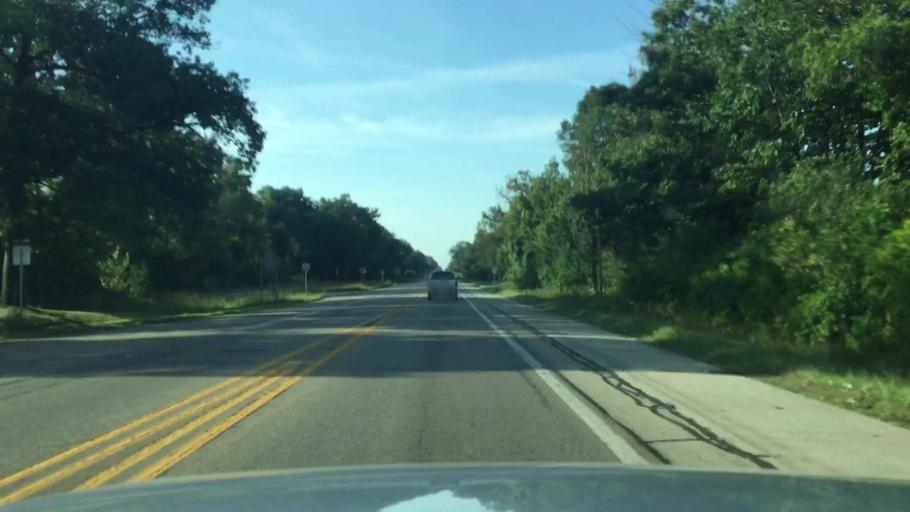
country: US
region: Michigan
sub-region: Jackson County
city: Vandercook Lake
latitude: 42.1156
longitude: -84.3641
